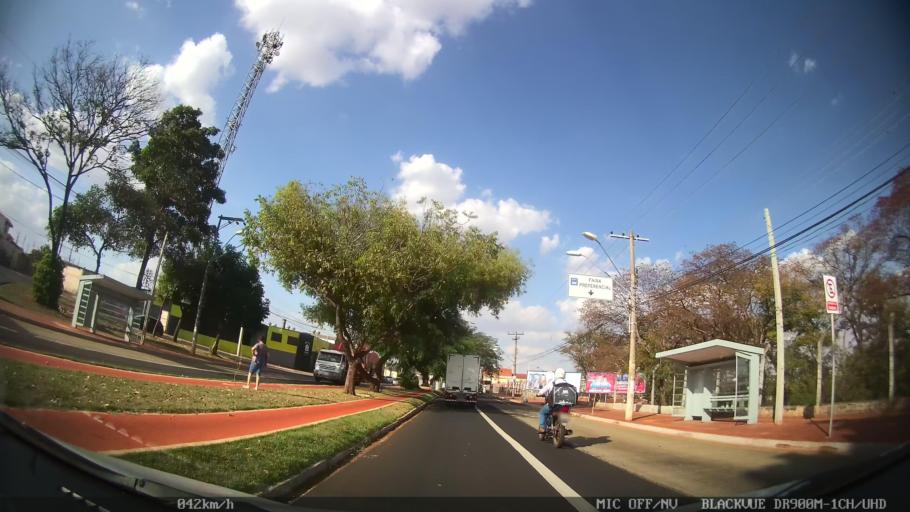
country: BR
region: Sao Paulo
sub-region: Ribeirao Preto
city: Ribeirao Preto
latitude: -21.1749
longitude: -47.8280
